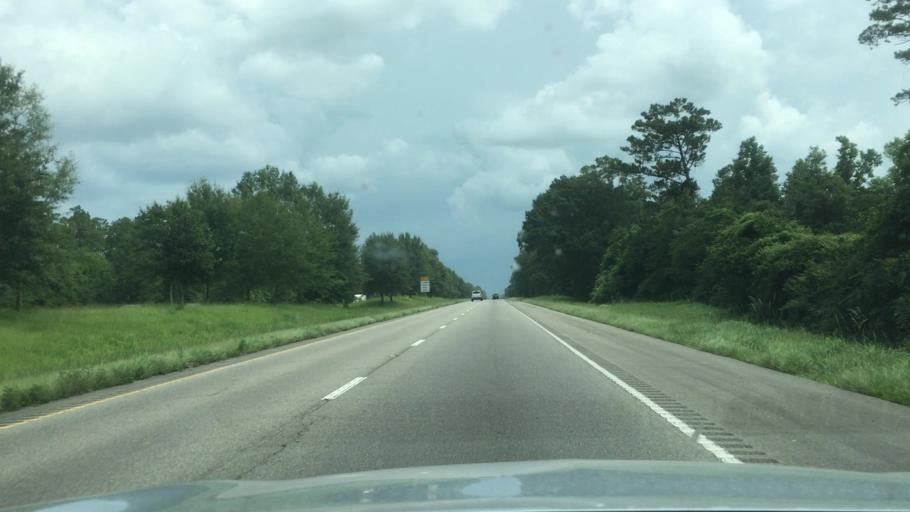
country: US
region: Mississippi
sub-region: Pearl River County
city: Carriere
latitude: 30.5710
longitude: -89.6342
